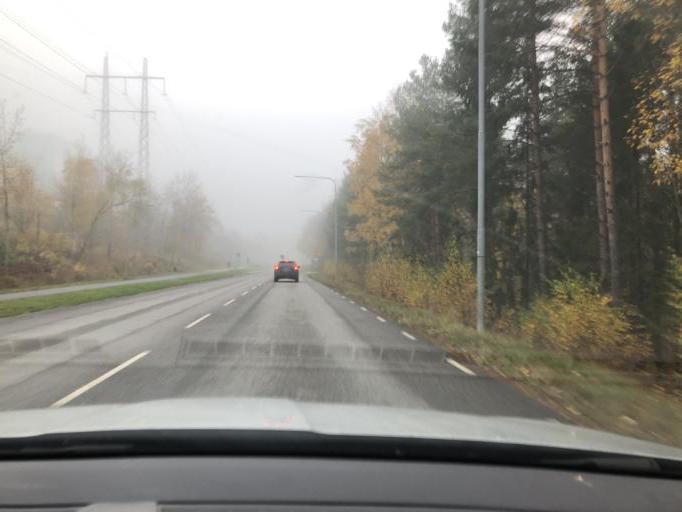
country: SE
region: Stockholm
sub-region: Huddinge Kommun
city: Huddinge
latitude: 59.2252
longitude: 17.9423
